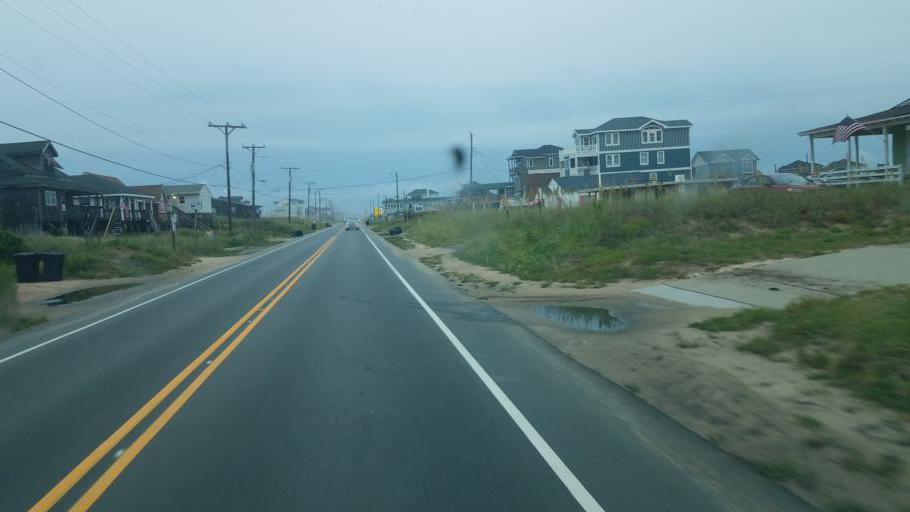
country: US
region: North Carolina
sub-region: Dare County
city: Kill Devil Hills
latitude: 36.0459
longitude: -75.6766
